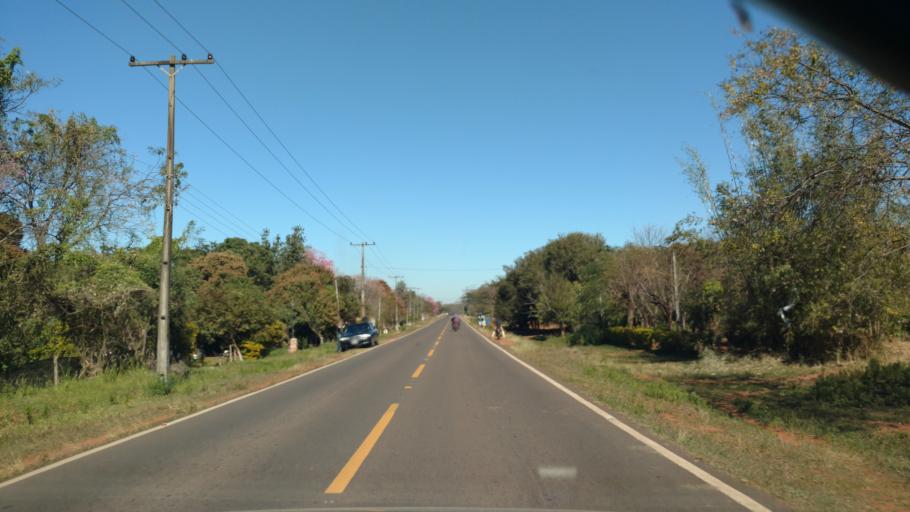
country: PY
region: Paraguari
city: Pirayu
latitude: -25.5202
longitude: -57.2644
